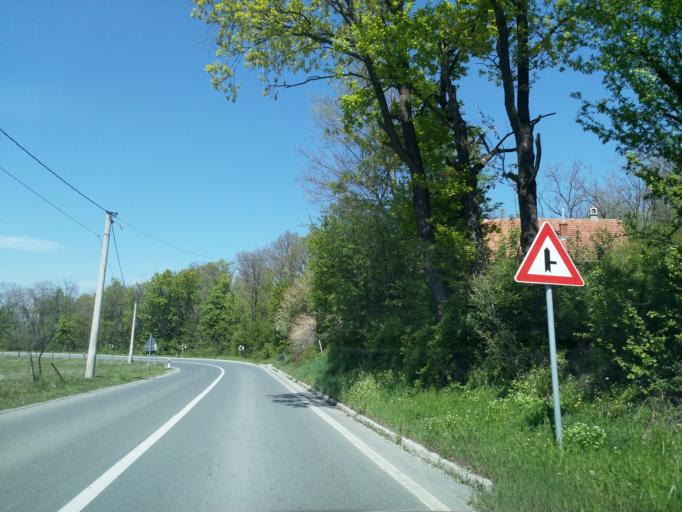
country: RS
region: Central Serbia
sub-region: Belgrade
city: Lazarevac
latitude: 44.3731
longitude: 20.3126
